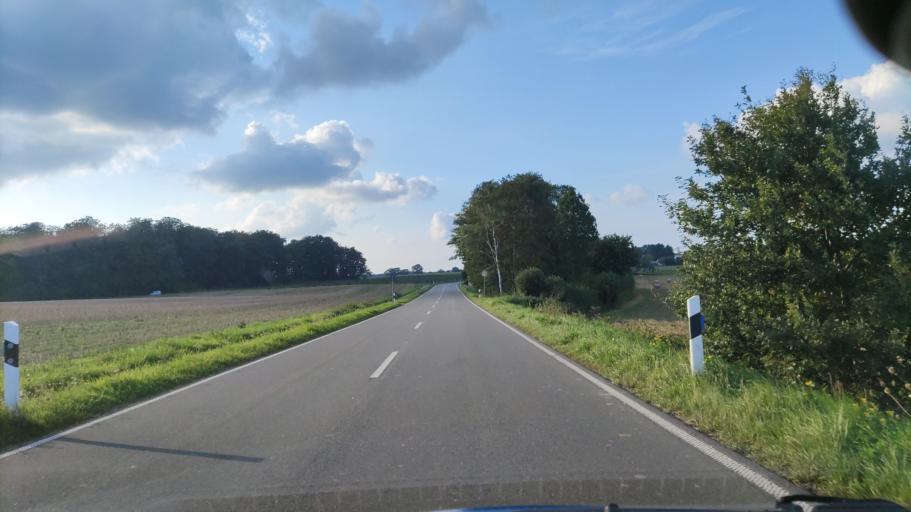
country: DE
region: Schleswig-Holstein
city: Glasau
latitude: 54.0418
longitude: 10.5353
